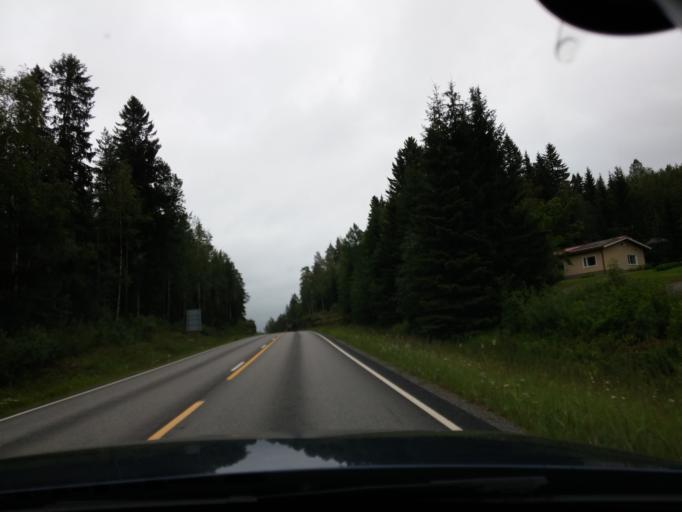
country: FI
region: Central Finland
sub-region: Saarijaervi-Viitasaari
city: Saarijaervi
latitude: 62.6888
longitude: 25.2671
